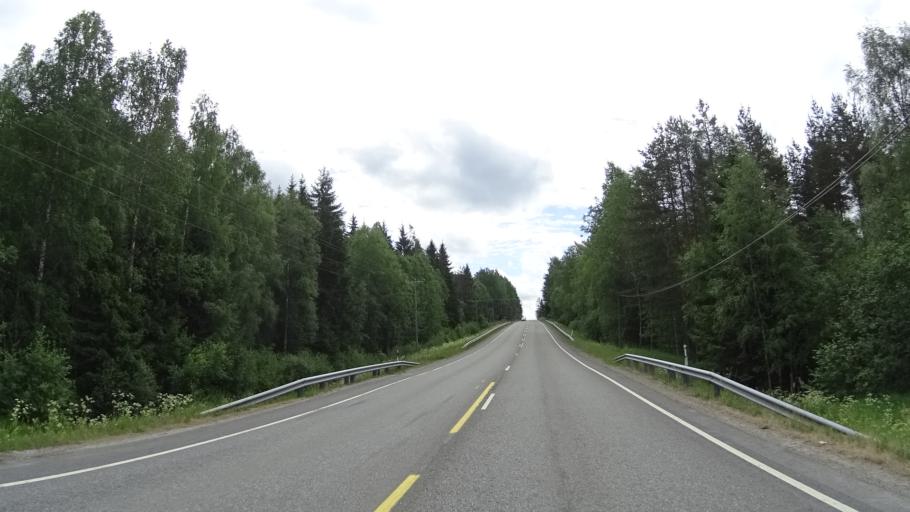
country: FI
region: Uusimaa
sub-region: Helsinki
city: Vihti
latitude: 60.2962
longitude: 24.3870
